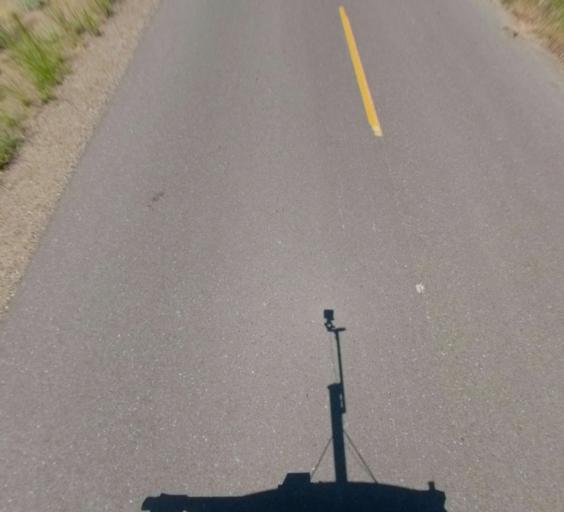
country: US
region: California
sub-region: Madera County
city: Madera Acres
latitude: 37.0686
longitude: -120.0047
